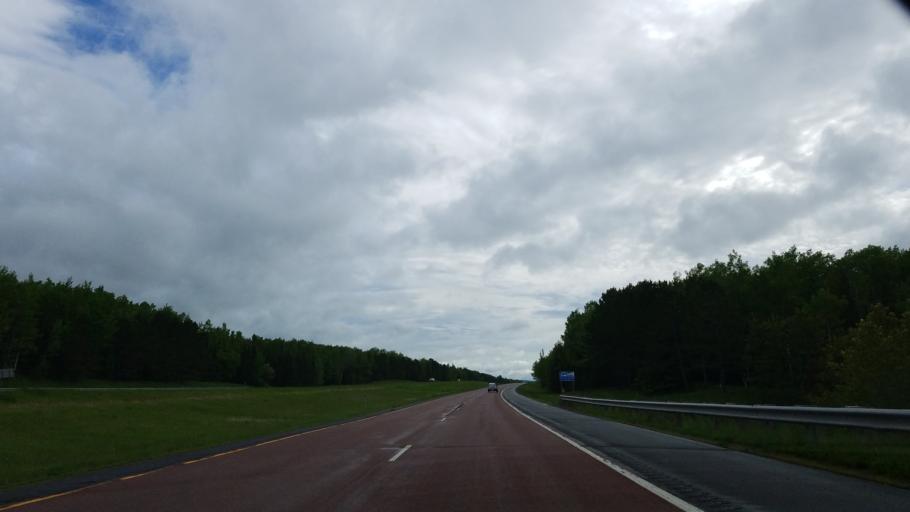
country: US
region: Minnesota
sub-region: Saint Louis County
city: Arnold
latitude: 46.9073
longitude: -91.8907
